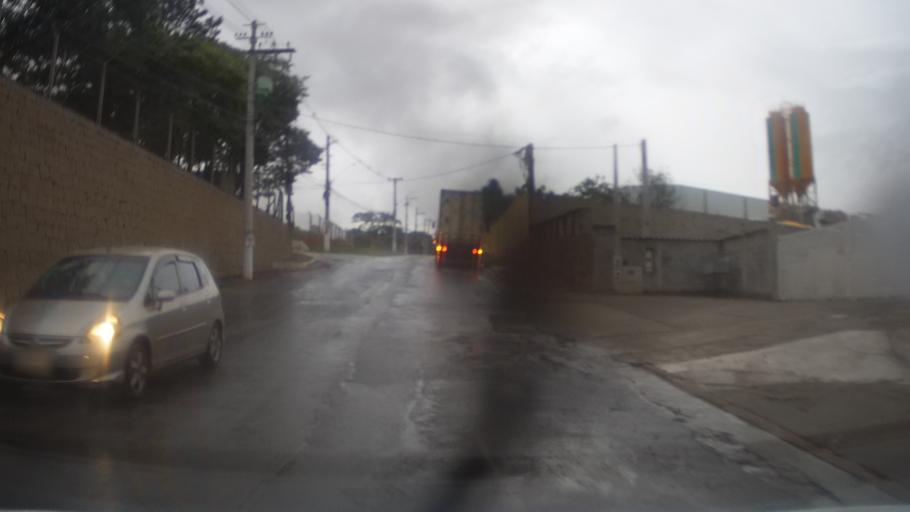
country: BR
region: Sao Paulo
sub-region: Itupeva
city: Itupeva
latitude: -23.1652
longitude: -47.0229
